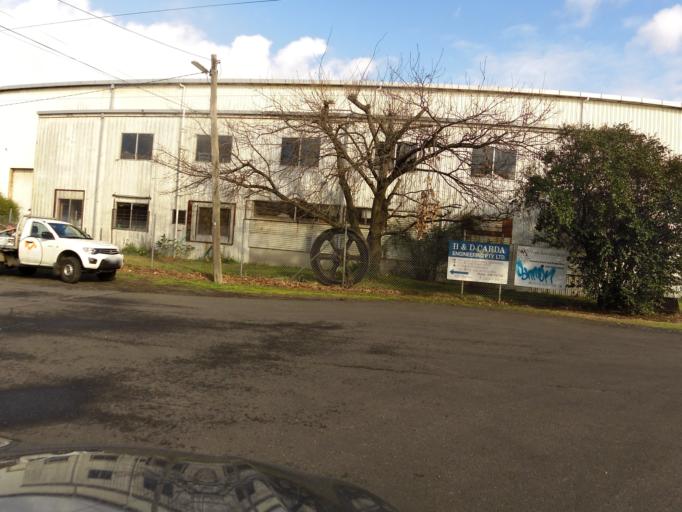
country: AU
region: Victoria
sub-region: Maribyrnong
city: Kingsville
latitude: -37.8063
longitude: 144.8663
